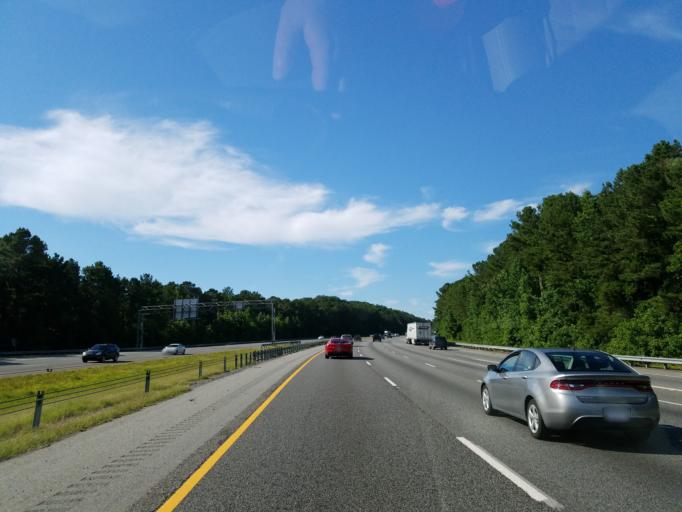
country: US
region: Georgia
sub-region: Bartow County
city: Emerson
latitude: 34.1226
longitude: -84.7405
